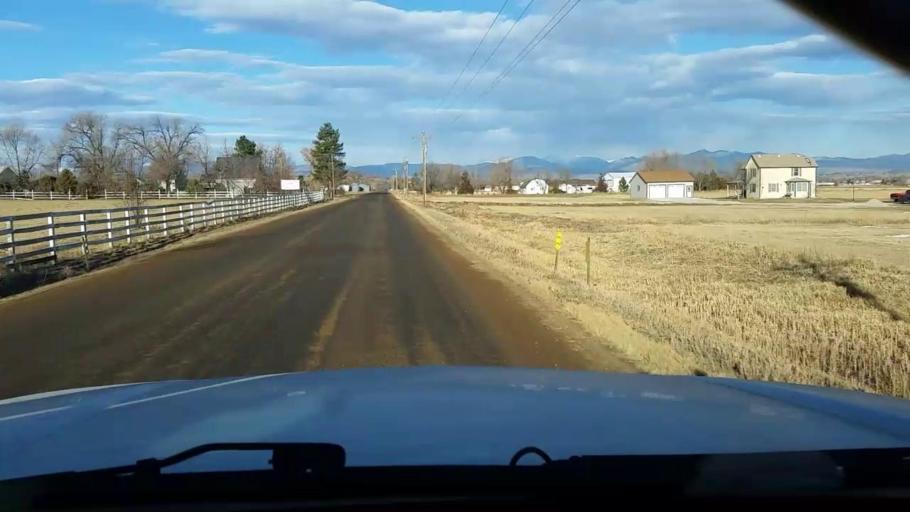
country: US
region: Colorado
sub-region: Larimer County
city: Campion
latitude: 40.3711
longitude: -105.0520
